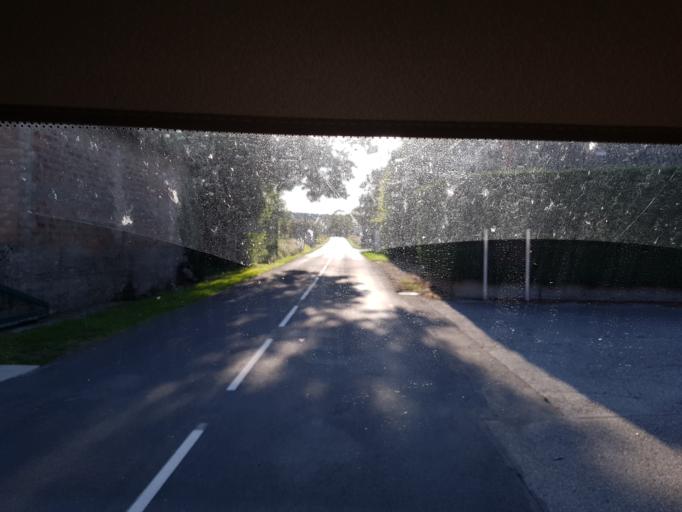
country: FR
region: Rhone-Alpes
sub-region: Departement de l'Ain
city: Priay
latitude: 46.0295
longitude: 5.2989
